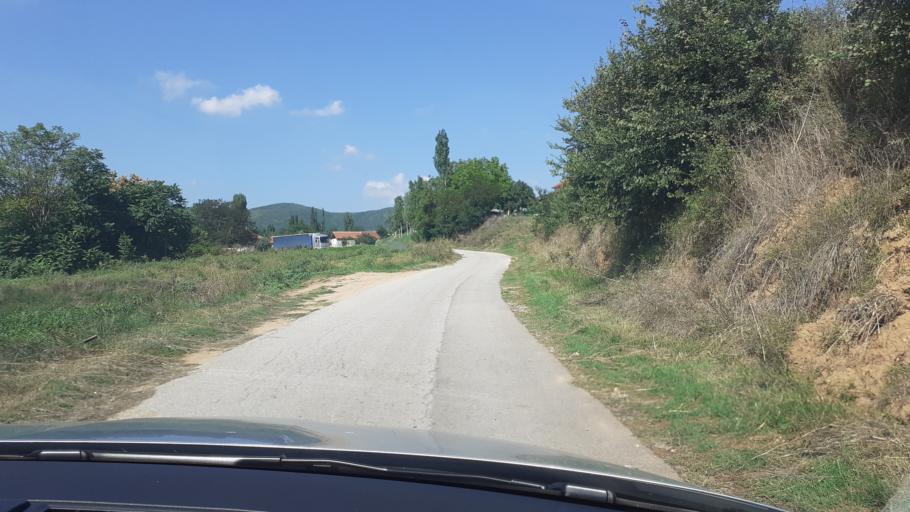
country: MK
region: Strumica
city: Veljusa
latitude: 41.5201
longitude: 22.5960
